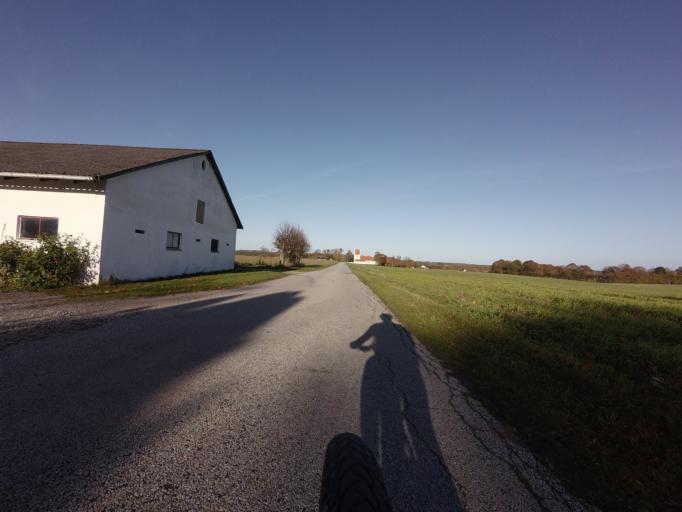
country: DK
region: Central Jutland
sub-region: Syddjurs Kommune
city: Ryomgard
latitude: 56.4583
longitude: 10.6306
